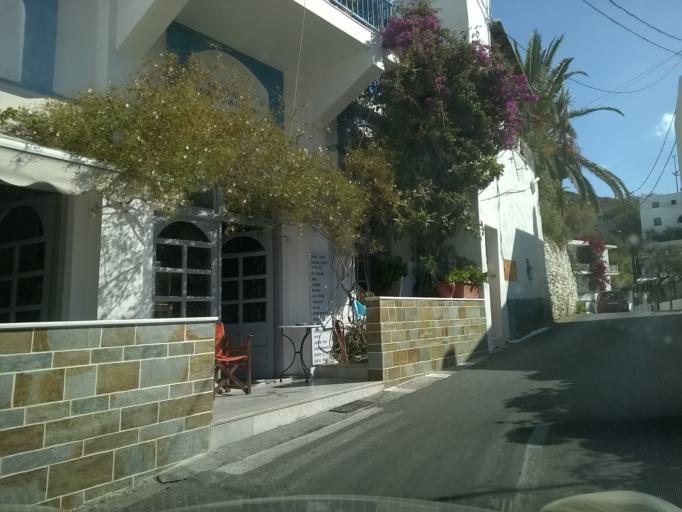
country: GR
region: South Aegean
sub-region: Nomos Kykladon
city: Filotion
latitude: 37.1013
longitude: 25.4793
